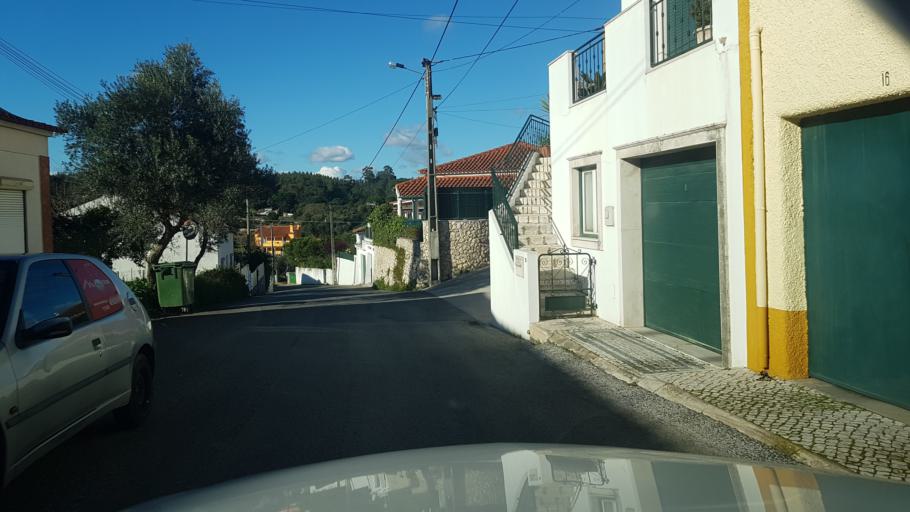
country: PT
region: Santarem
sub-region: Entroncamento
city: Entroncamento
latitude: 39.4769
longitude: -8.4986
